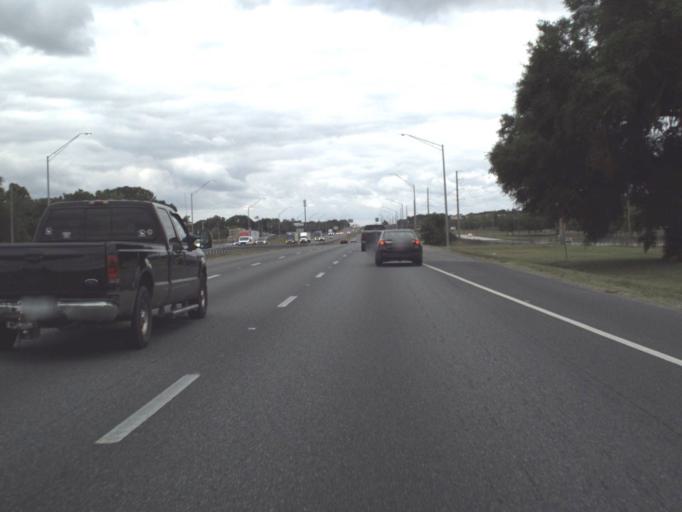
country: US
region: Florida
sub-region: Marion County
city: Ocala
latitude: 29.1797
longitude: -82.1850
